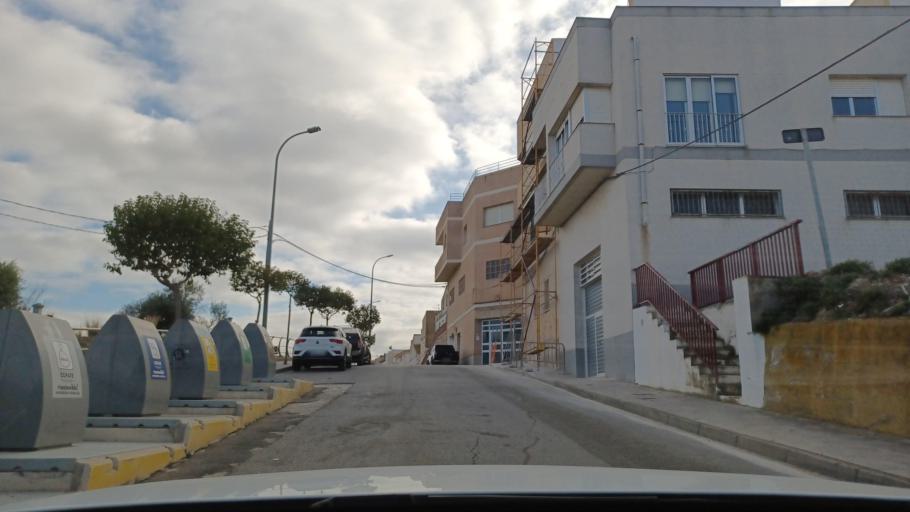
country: ES
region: Catalonia
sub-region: Provincia de Tarragona
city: Amposta
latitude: 40.7161
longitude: 0.5750
